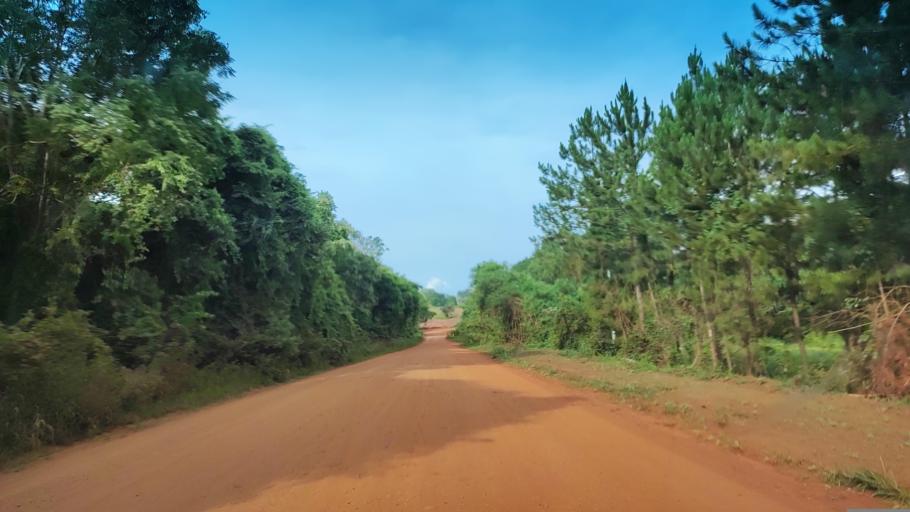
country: AR
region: Misiones
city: Gobernador Roca
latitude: -27.1383
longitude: -55.5206
